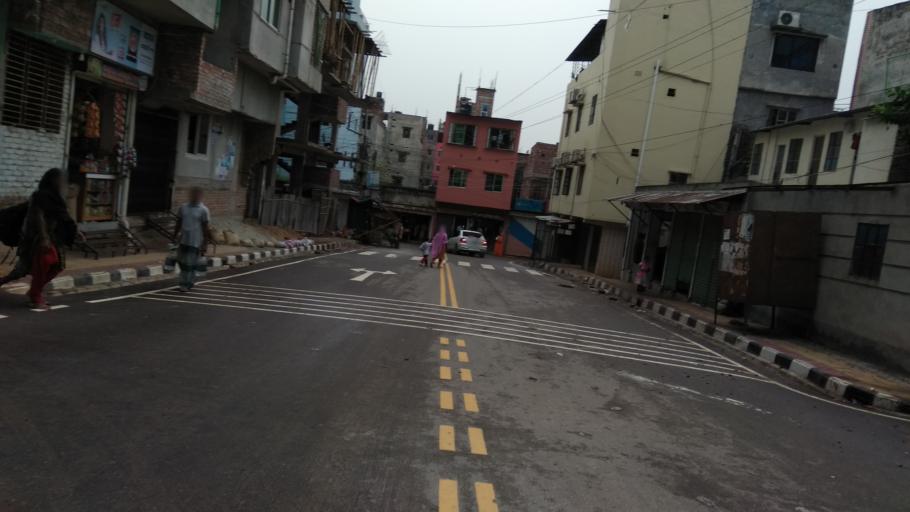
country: BD
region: Dhaka
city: Tungi
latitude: 23.8277
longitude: 90.3727
